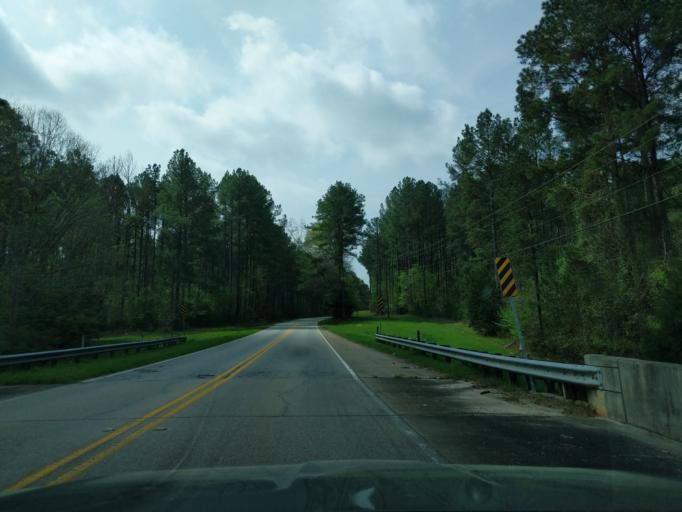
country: US
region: Georgia
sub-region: Columbia County
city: Appling
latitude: 33.5752
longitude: -82.3185
